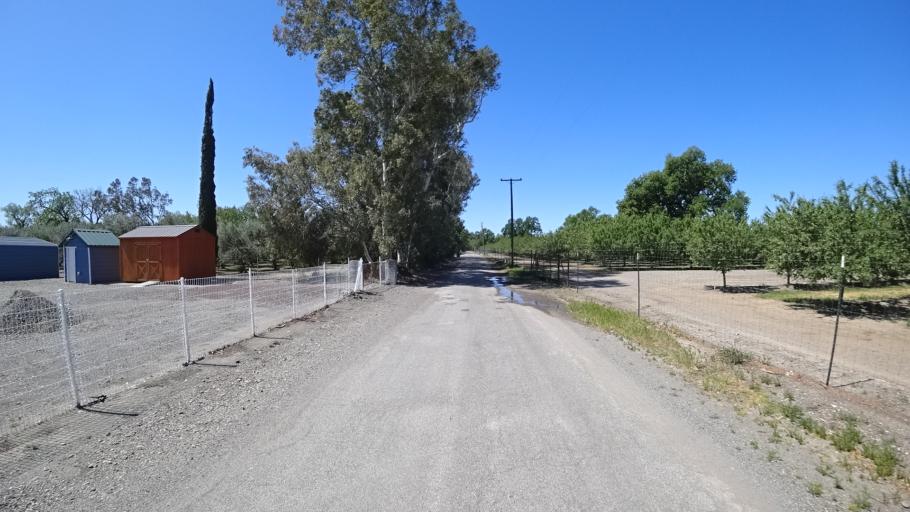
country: US
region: California
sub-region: Glenn County
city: Orland
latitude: 39.7914
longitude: -122.2344
